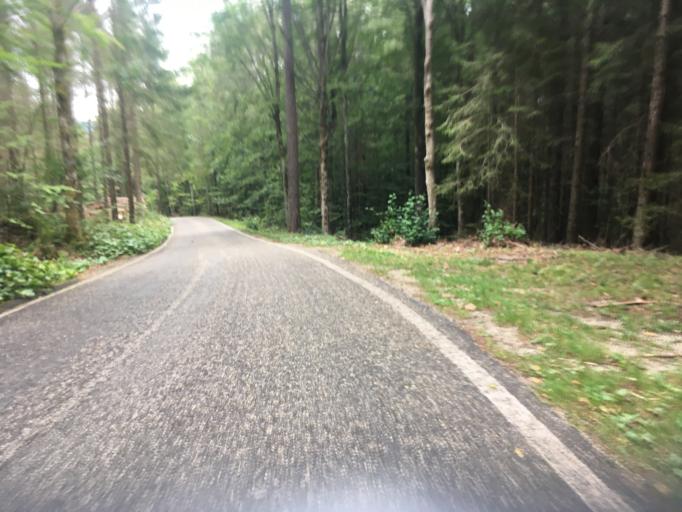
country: CH
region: Solothurn
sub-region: Bezirk Thal
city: Welschenrohr
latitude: 47.2609
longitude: 7.4892
